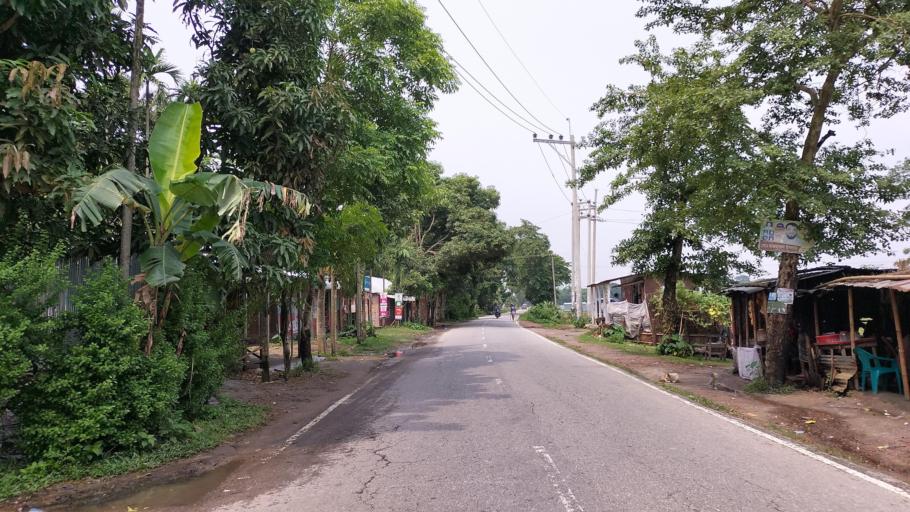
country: BD
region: Dhaka
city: Netrakona
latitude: 24.9050
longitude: 90.7659
